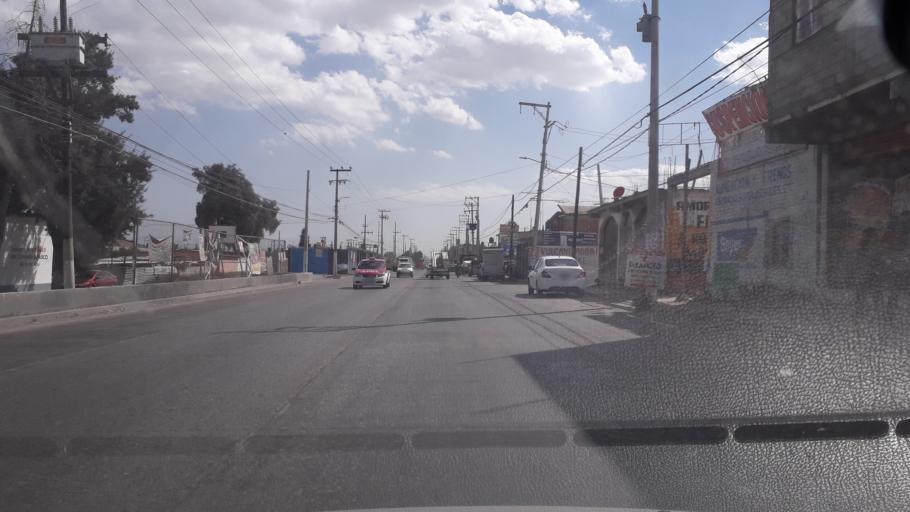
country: MX
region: Mexico
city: Ecatepec
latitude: 19.6332
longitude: -99.0538
